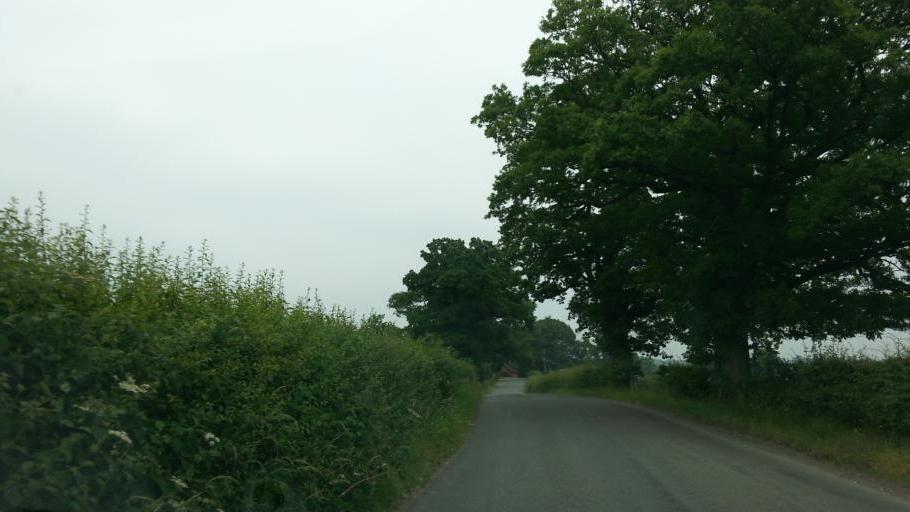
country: GB
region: England
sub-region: Staffordshire
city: Colwich
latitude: 52.8342
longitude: -1.9819
